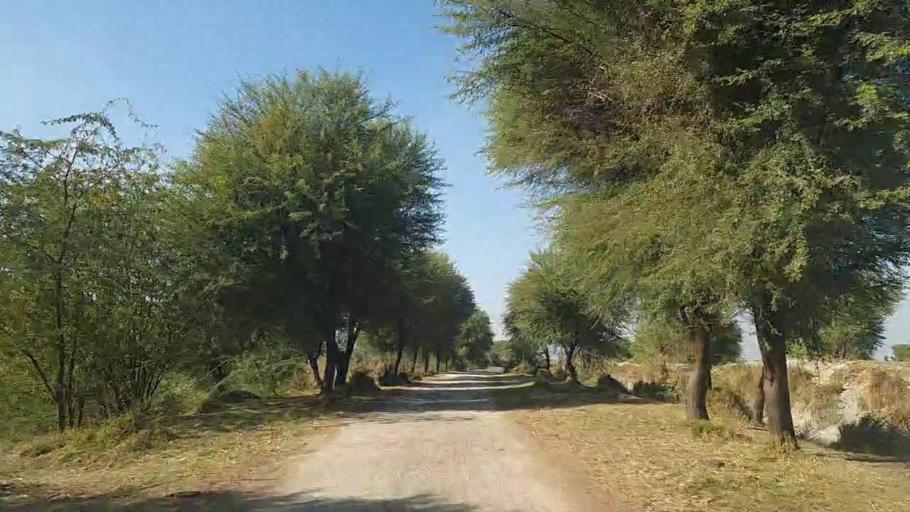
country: PK
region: Sindh
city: Shahpur Chakar
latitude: 26.2156
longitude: 68.6068
